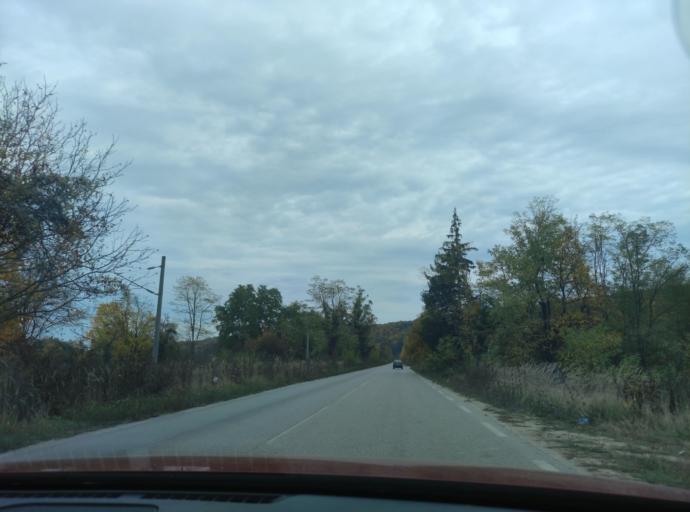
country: BG
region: Montana
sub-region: Obshtina Berkovitsa
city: Berkovitsa
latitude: 43.2553
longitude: 23.1721
